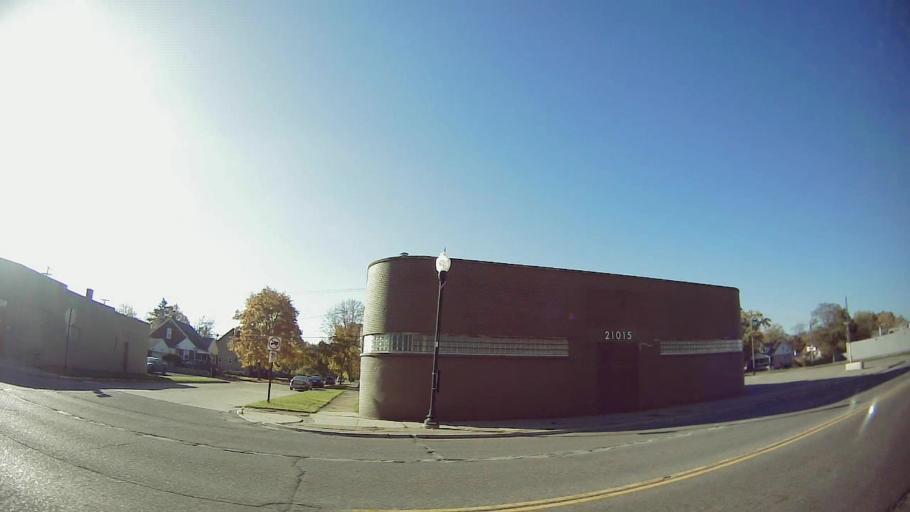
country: US
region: Michigan
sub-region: Oakland County
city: Hazel Park
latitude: 42.4471
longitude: -83.1027
